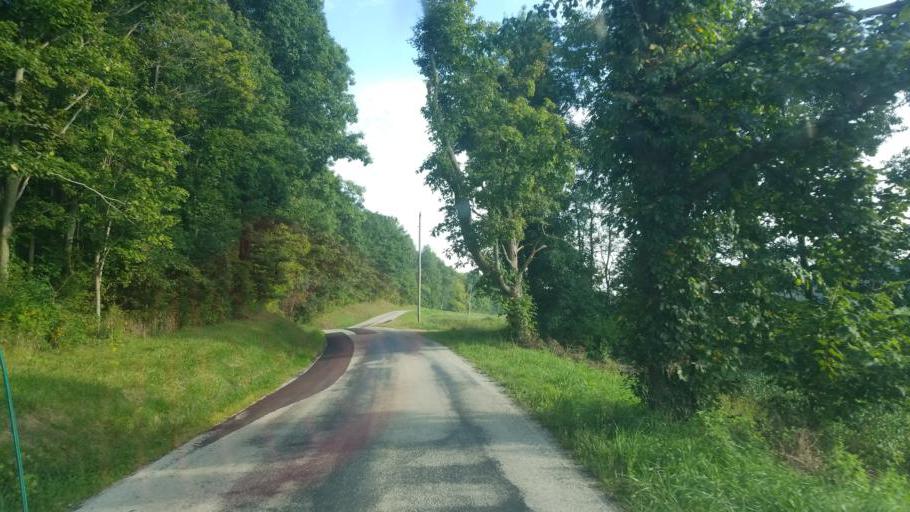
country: US
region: Ohio
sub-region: Medina County
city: Lodi
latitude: 40.9382
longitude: -82.0117
